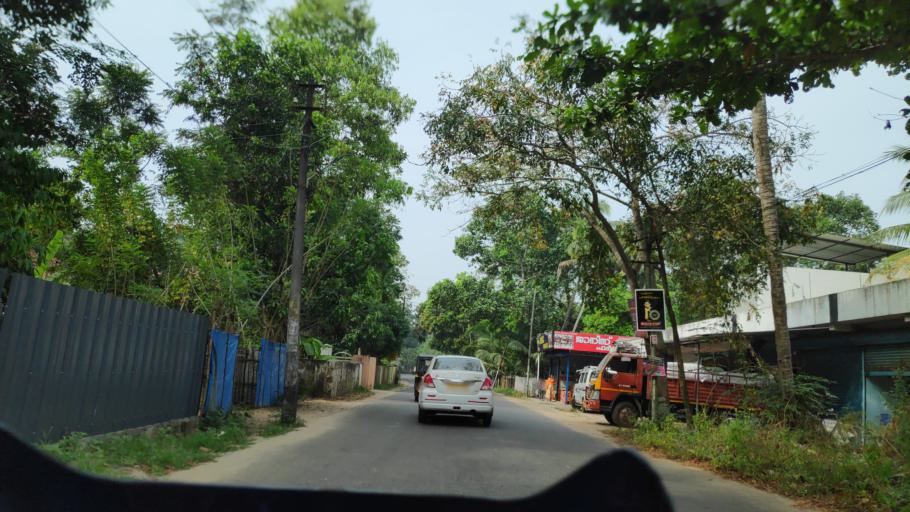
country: IN
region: Kerala
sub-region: Alappuzha
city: Kutiatodu
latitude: 9.8207
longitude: 76.3493
